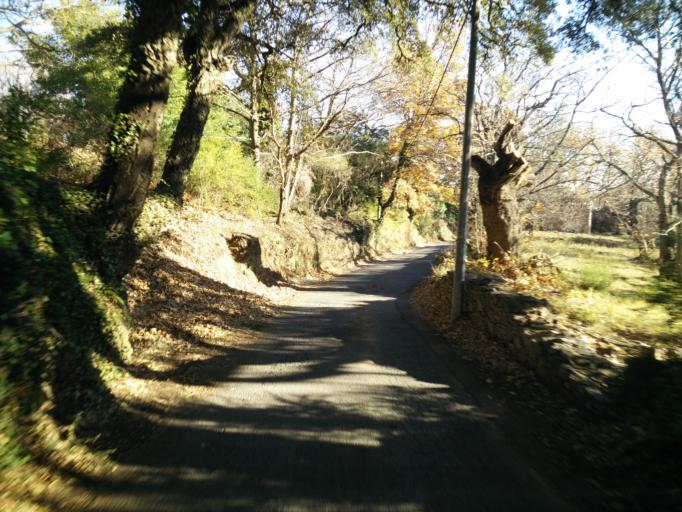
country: FR
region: Provence-Alpes-Cote d'Azur
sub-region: Departement du Var
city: La Garde-Freinet
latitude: 43.3100
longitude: 6.4776
